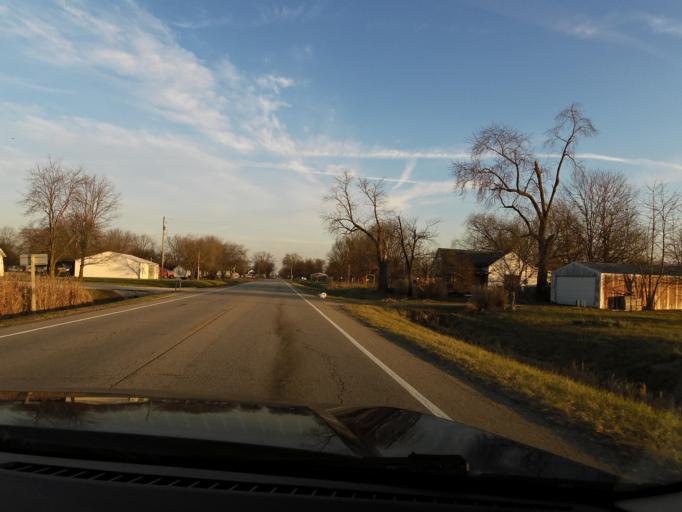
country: US
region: Illinois
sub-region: Fayette County
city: Vandalia
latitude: 38.7987
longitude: -89.0864
